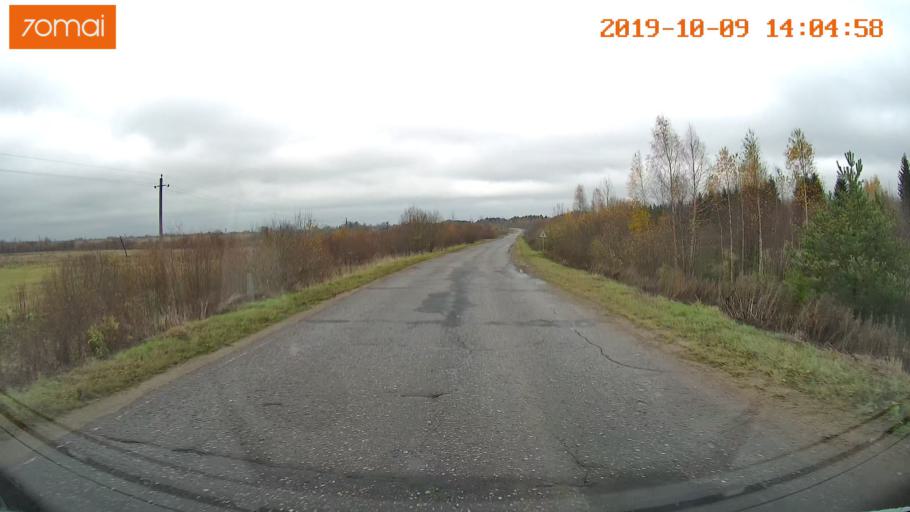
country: RU
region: Kostroma
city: Buy
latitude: 58.4589
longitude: 41.3890
